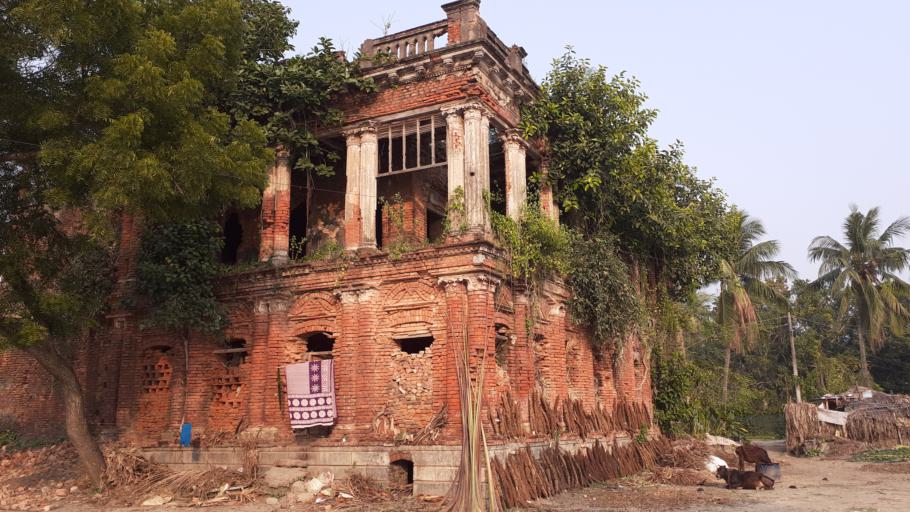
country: IN
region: West Bengal
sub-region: North 24 Parganas
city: Taki
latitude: 22.3366
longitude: 89.1174
